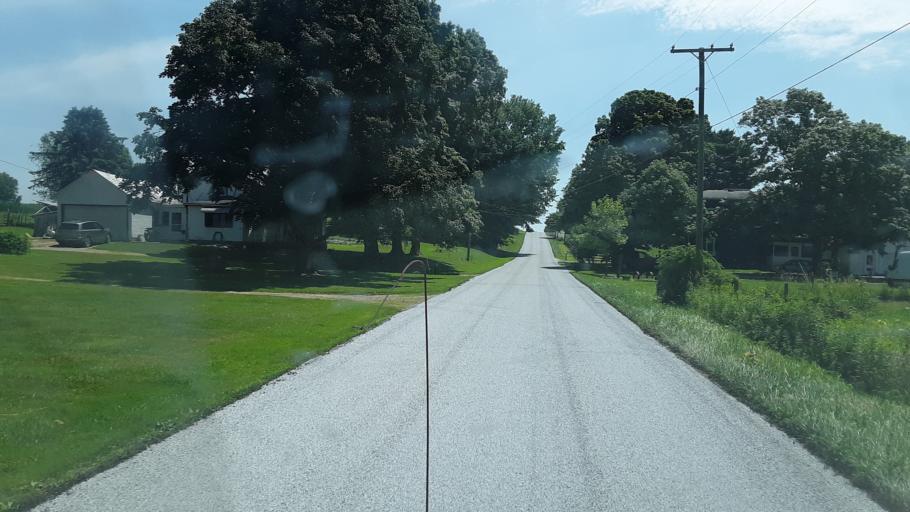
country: US
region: Ohio
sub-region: Wayne County
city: Shreve
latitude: 40.7192
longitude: -81.9641
